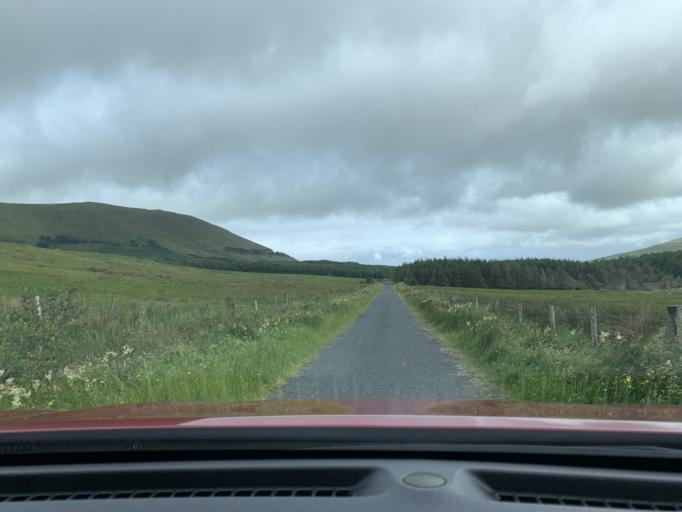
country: IE
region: Connaught
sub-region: Sligo
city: Sligo
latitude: 54.3730
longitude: -8.4154
